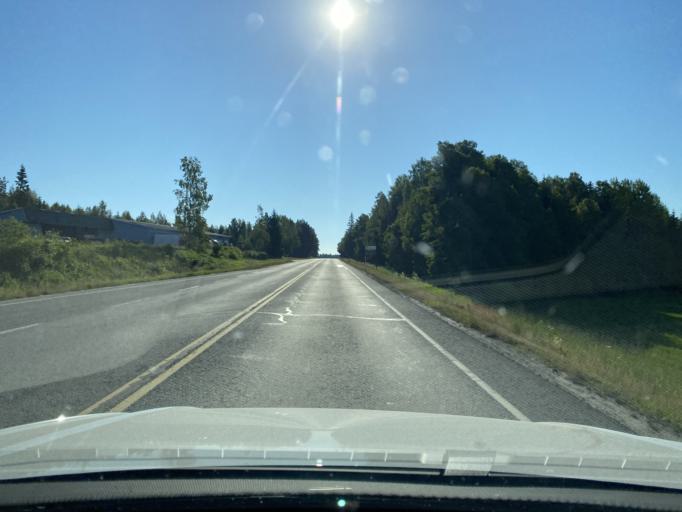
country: FI
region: Haeme
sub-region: Forssa
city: Forssa
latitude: 60.8301
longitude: 23.6942
